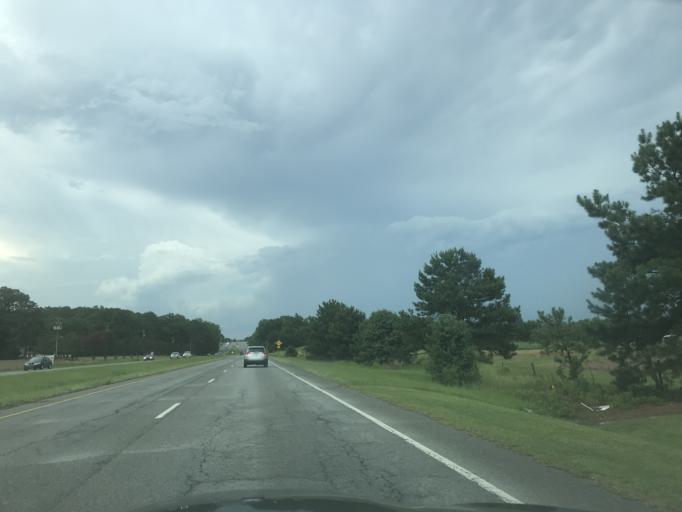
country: US
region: North Carolina
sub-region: Johnston County
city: Clayton
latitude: 35.6690
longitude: -78.5053
